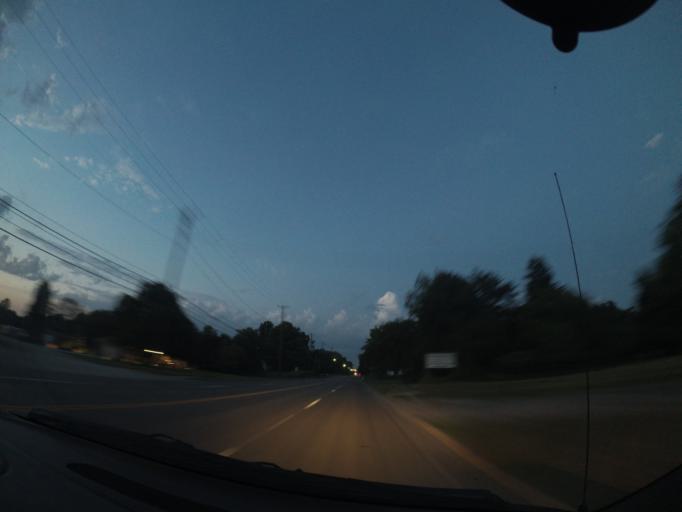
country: US
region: Ohio
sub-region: Ashtabula County
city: Geneva
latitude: 41.8197
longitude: -80.8937
